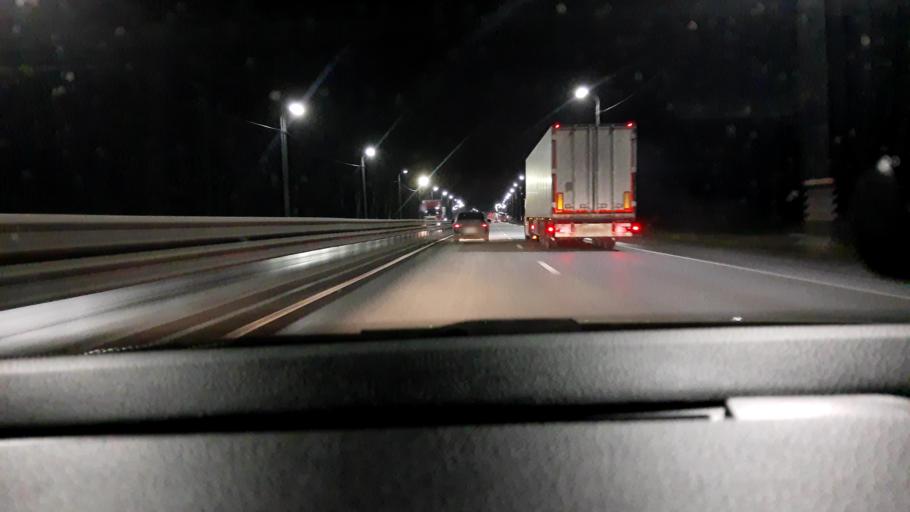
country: RU
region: Moskovskaya
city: Malaya Dubna
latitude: 55.8899
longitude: 39.0196
